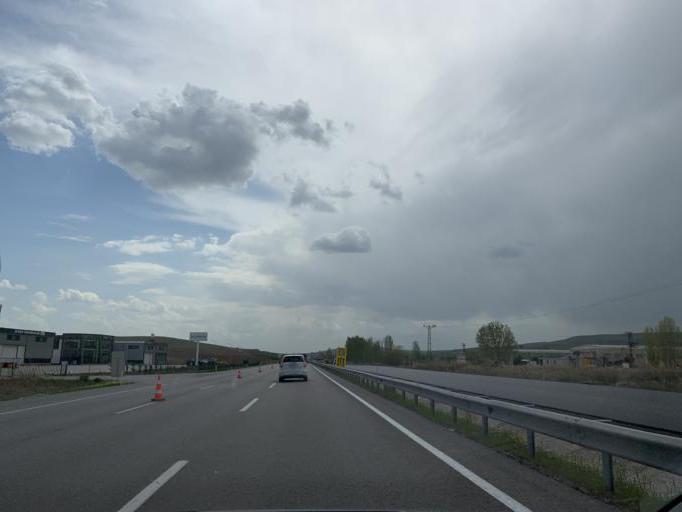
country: TR
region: Ankara
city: Polatli
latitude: 39.6425
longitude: 32.2067
